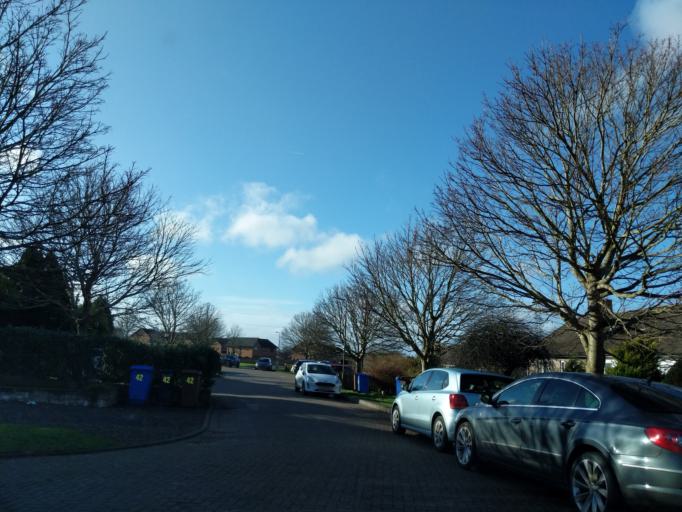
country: GB
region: Scotland
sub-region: West Lothian
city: Kirknewton
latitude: 55.8892
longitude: -3.4205
